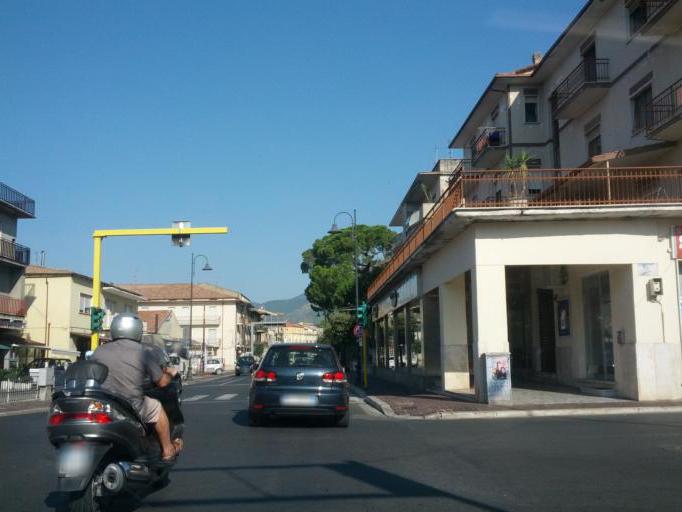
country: IT
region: Latium
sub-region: Provincia di Latina
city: Fondi
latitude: 41.3540
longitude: 13.4320
